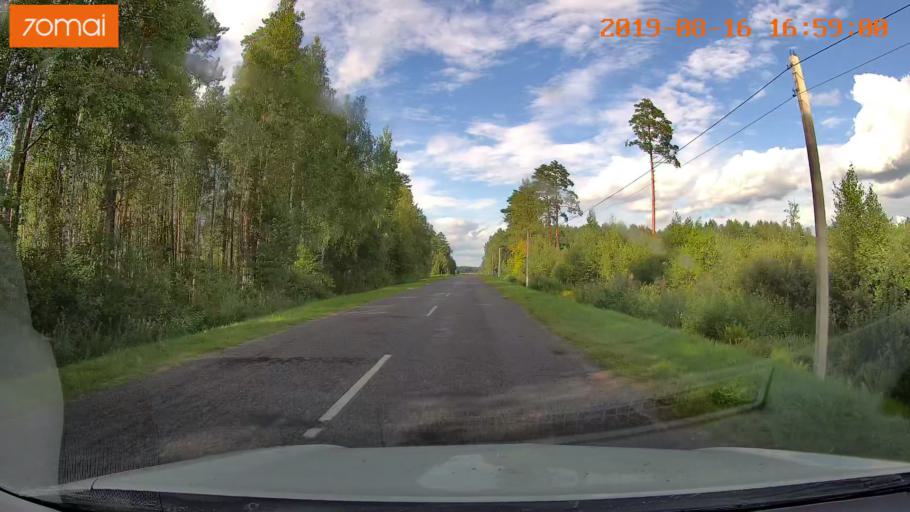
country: BY
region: Mogilev
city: Hlusha
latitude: 53.2770
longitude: 28.8384
